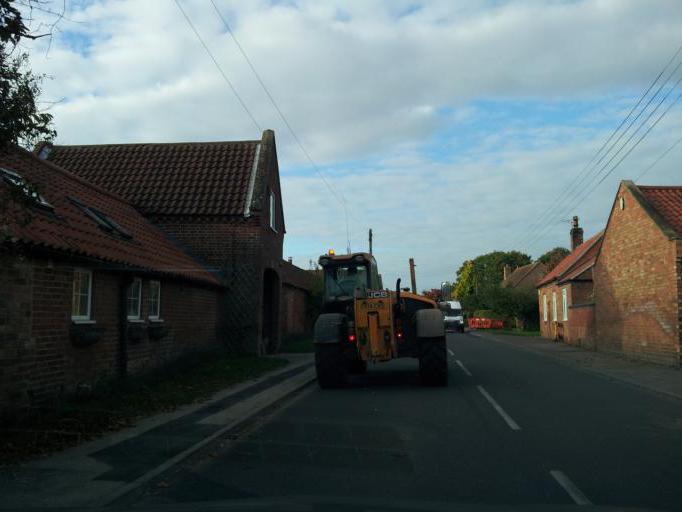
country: GB
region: England
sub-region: Lincolnshire
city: Long Bennington
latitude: 52.9717
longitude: -0.8205
